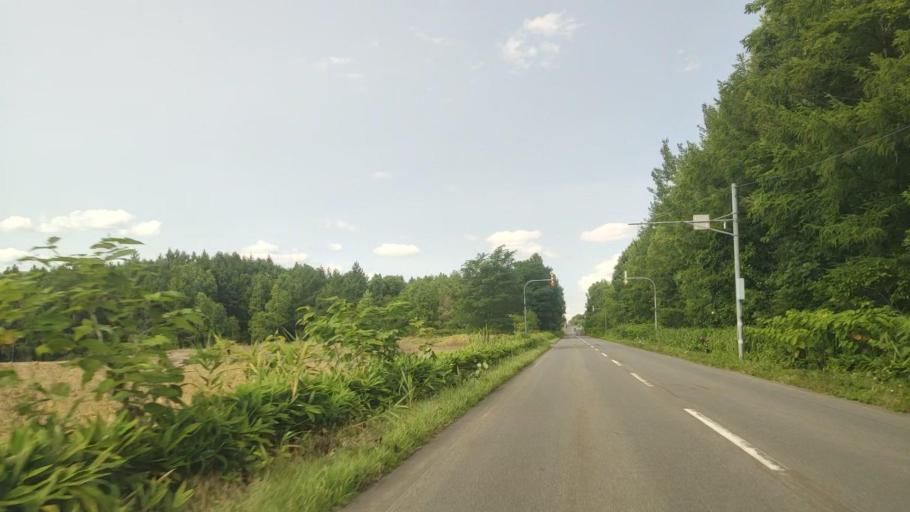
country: JP
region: Hokkaido
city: Nayoro
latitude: 44.2423
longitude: 142.4157
